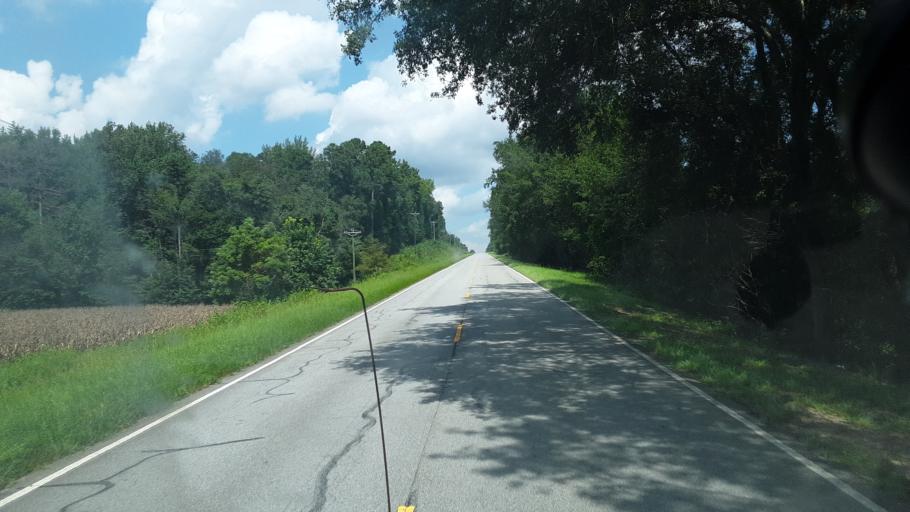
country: US
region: South Carolina
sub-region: Calhoun County
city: Oak Grove
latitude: 33.7386
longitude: -80.9587
